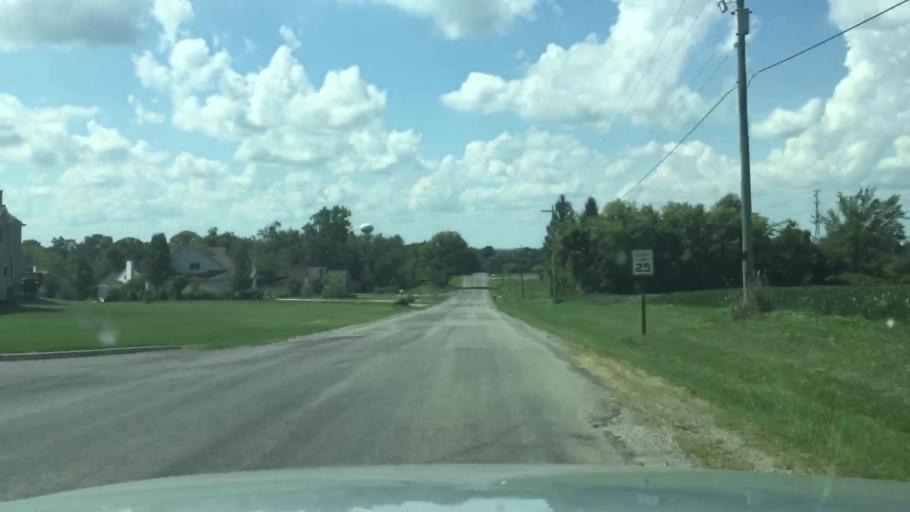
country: US
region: Michigan
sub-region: Lenawee County
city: Clinton
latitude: 42.0725
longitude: -83.9526
